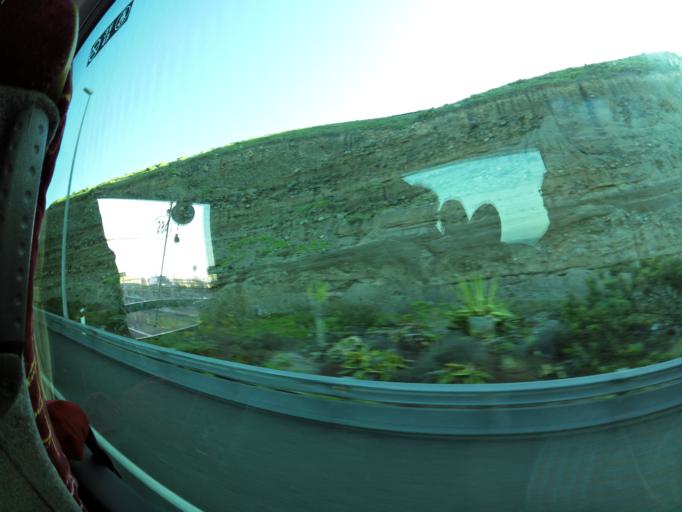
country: ES
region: Canary Islands
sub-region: Provincia de Las Palmas
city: Las Palmas de Gran Canaria
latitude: 28.1267
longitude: -15.4531
